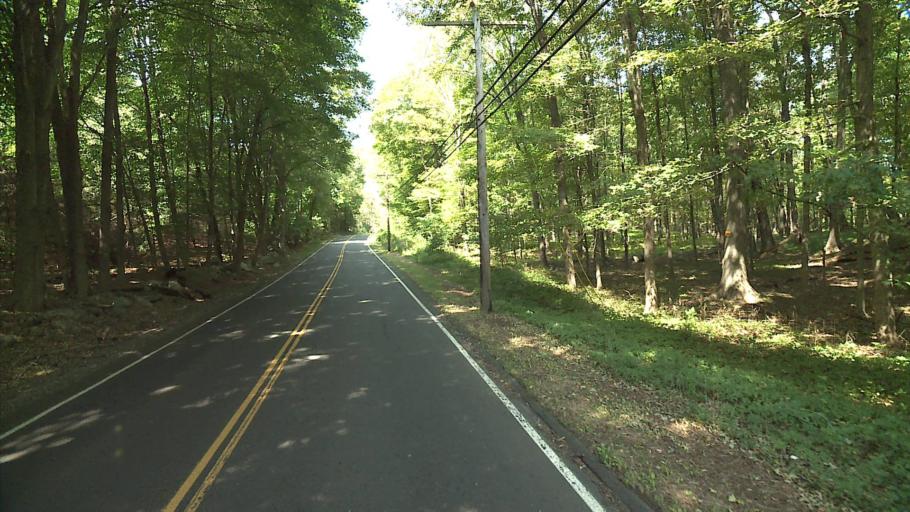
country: US
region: Connecticut
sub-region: Fairfield County
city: Georgetown
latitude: 41.2619
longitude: -73.3263
